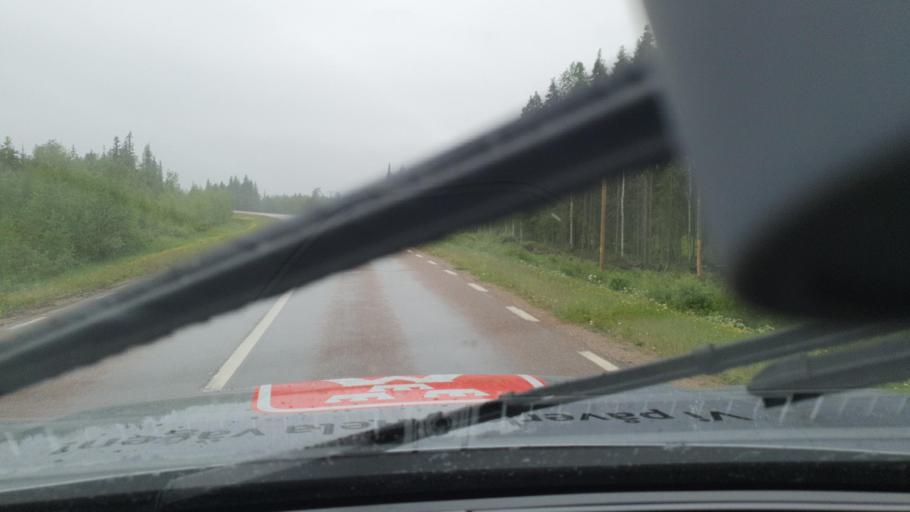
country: SE
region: Norrbotten
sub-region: Overtornea Kommun
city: OEvertornea
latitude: 66.4509
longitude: 23.2970
